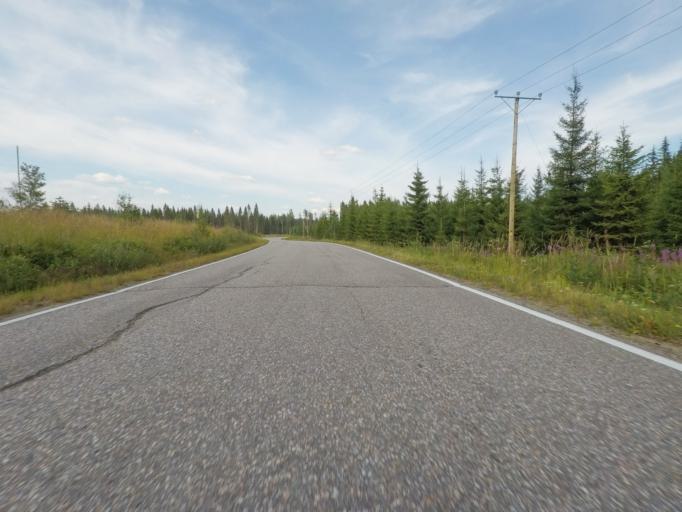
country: FI
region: Southern Savonia
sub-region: Savonlinna
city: Sulkava
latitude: 61.7472
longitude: 28.2006
